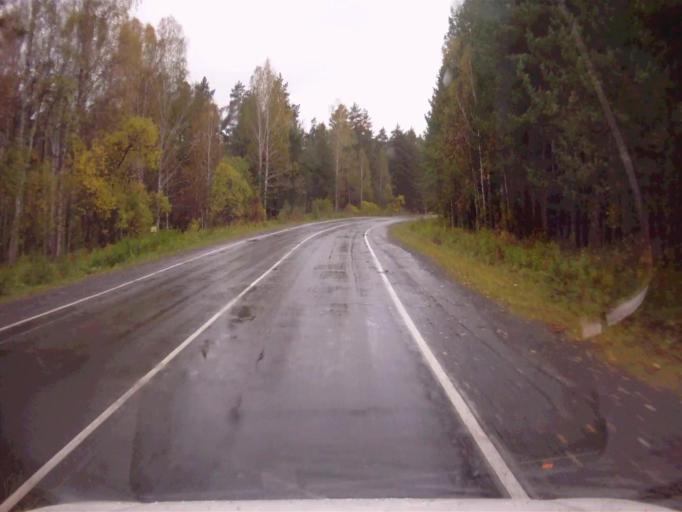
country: RU
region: Chelyabinsk
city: Verkhniy Ufaley
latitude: 55.9593
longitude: 60.3845
